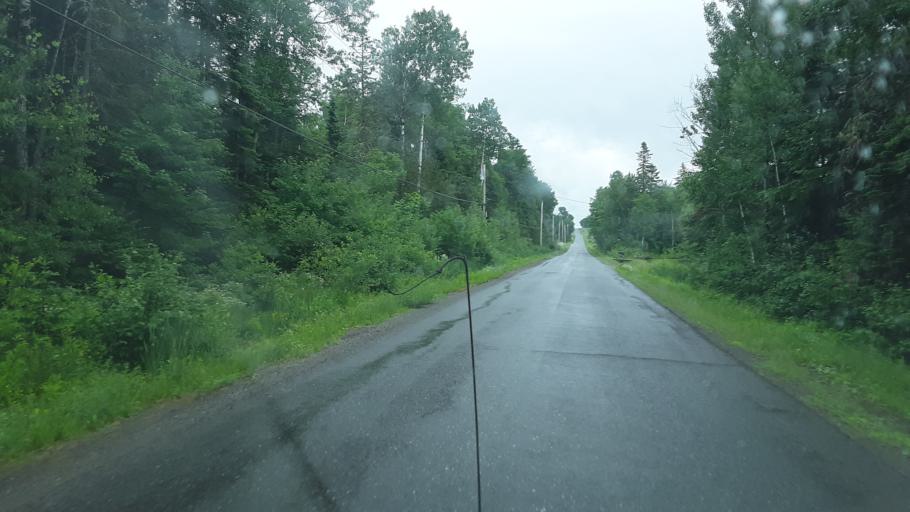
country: US
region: Maine
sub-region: Aroostook County
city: Presque Isle
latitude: 46.6815
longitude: -68.2003
